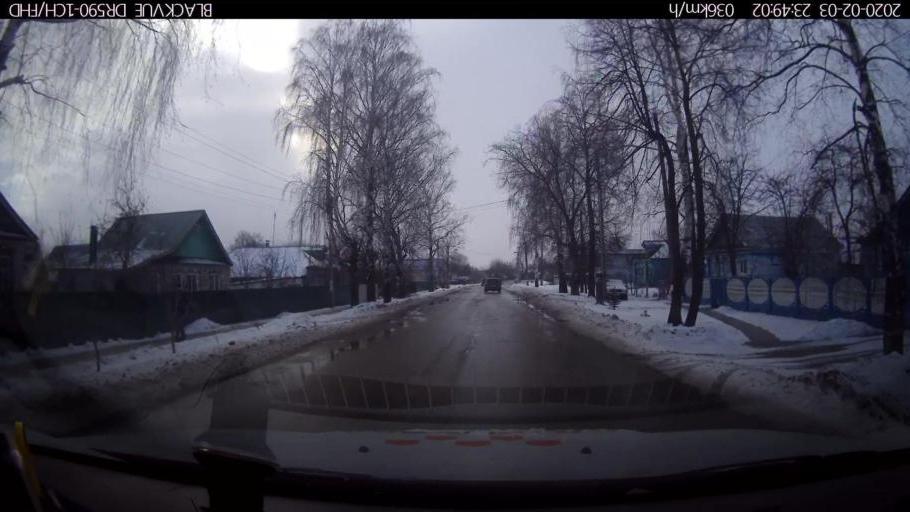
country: RU
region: Nizjnij Novgorod
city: Dal'neye Konstantinovo
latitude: 55.8100
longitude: 44.0897
